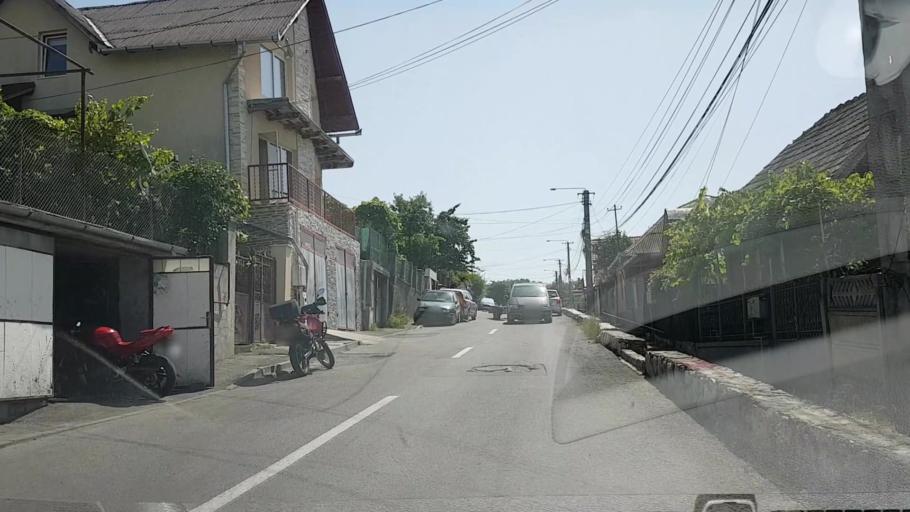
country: RO
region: Cluj
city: Turda
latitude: 46.5776
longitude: 23.7852
